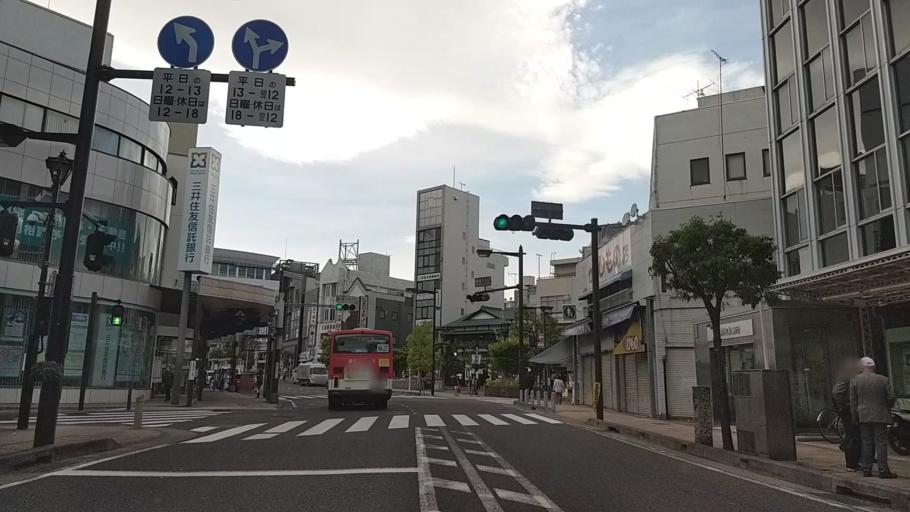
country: JP
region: Kanagawa
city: Odawara
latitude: 35.2548
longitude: 139.1579
